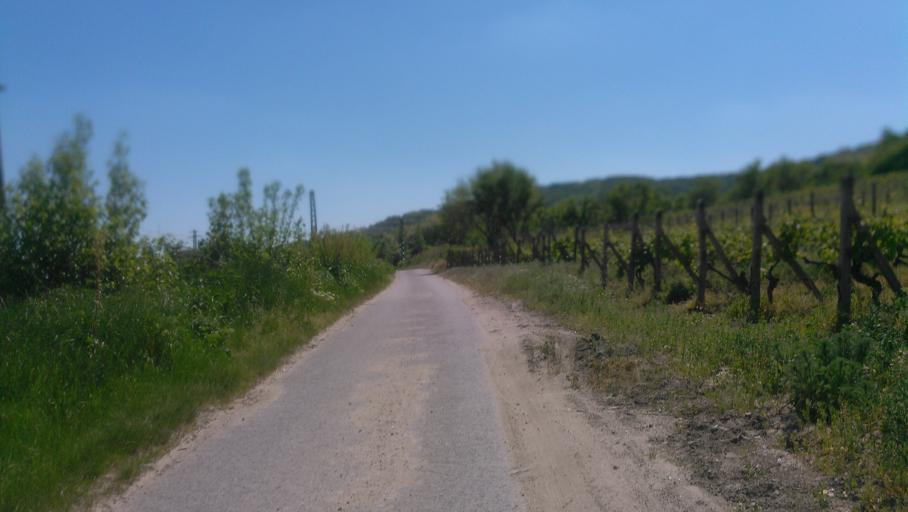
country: SK
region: Bratislavsky
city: Bratislava
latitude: 48.1823
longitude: 17.1247
